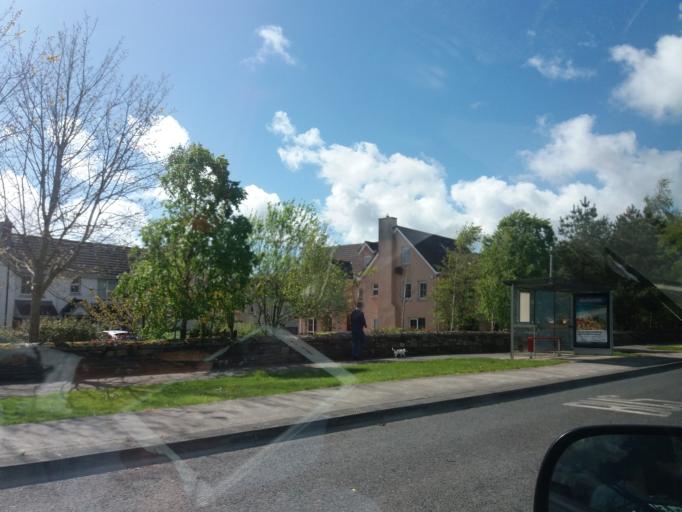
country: IE
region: Munster
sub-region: Waterford
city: Waterford
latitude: 52.2397
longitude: -7.0659
